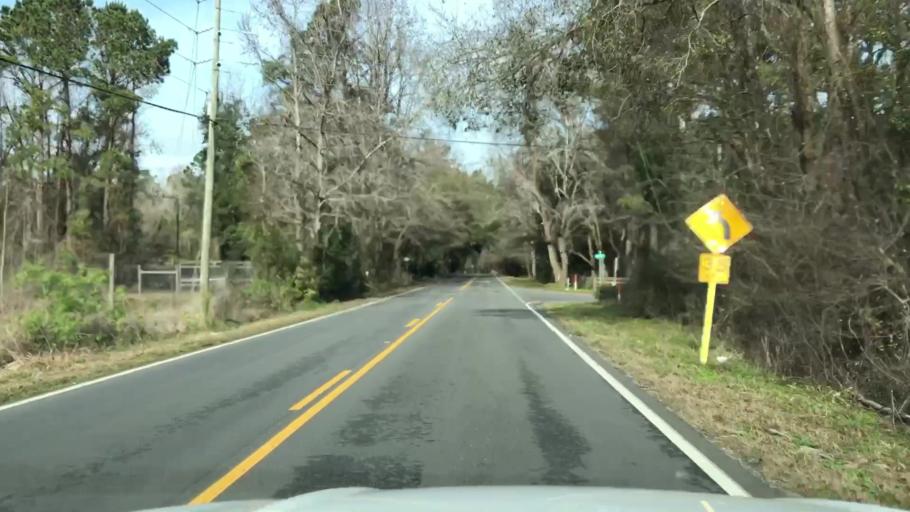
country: US
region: South Carolina
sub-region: Charleston County
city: Shell Point
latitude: 32.7241
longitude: -80.0233
